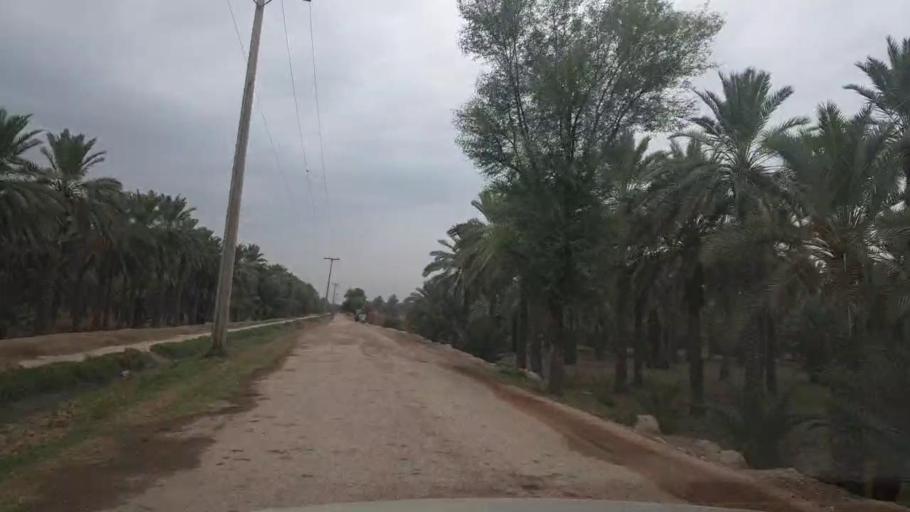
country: PK
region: Sindh
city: Khairpur
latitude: 27.6080
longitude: 68.8168
